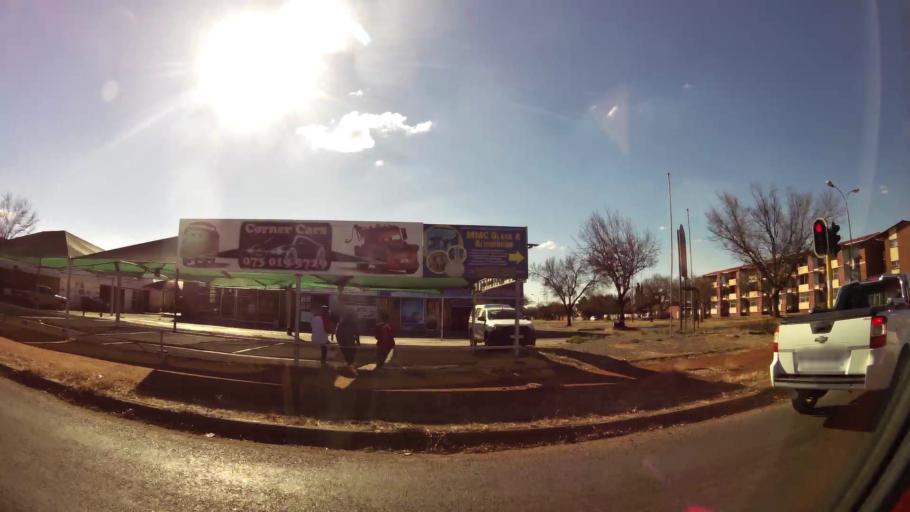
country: ZA
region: Gauteng
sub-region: West Rand District Municipality
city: Carletonville
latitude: -26.3571
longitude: 27.3907
